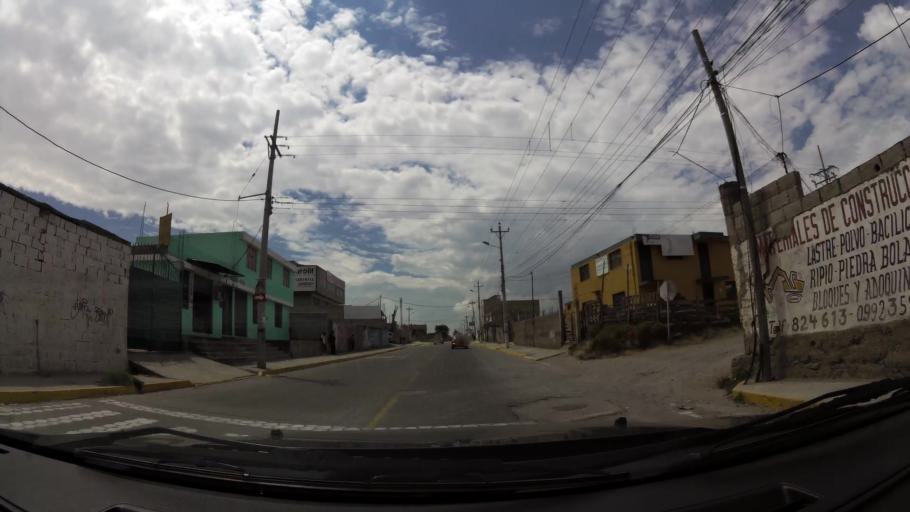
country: EC
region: Pichincha
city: Quito
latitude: -0.0712
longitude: -78.4153
